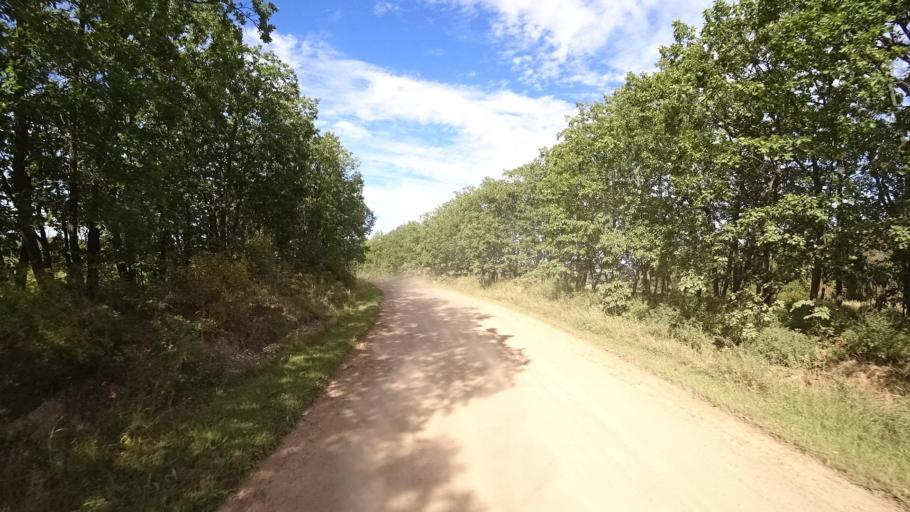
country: RU
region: Primorskiy
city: Yakovlevka
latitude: 44.4165
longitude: 133.5710
